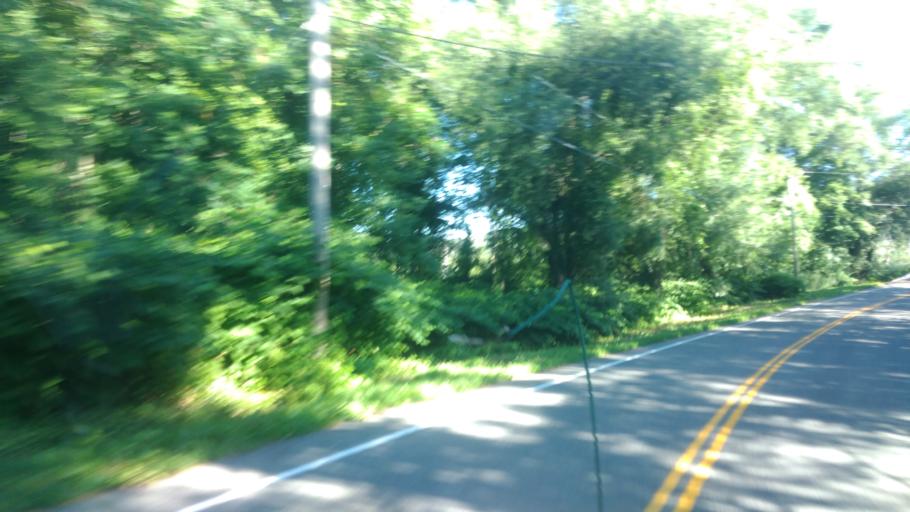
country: US
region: New York
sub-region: Wayne County
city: Sodus
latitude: 43.2232
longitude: -77.1118
